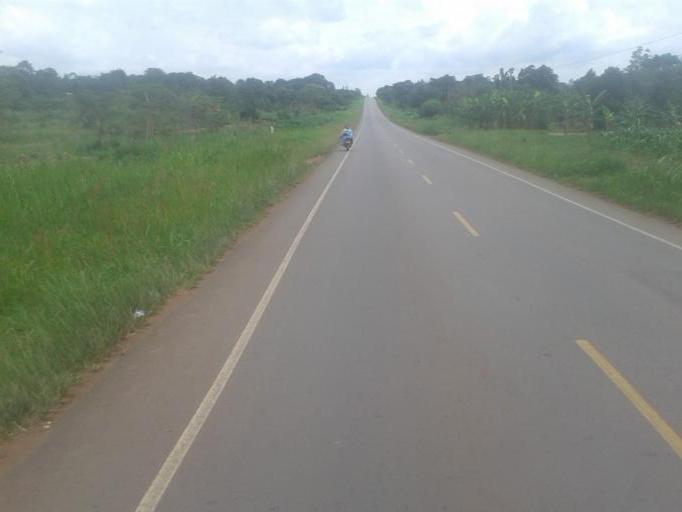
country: UG
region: Central Region
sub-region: Luwero District
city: Luwero
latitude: 0.8907
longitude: 32.4805
